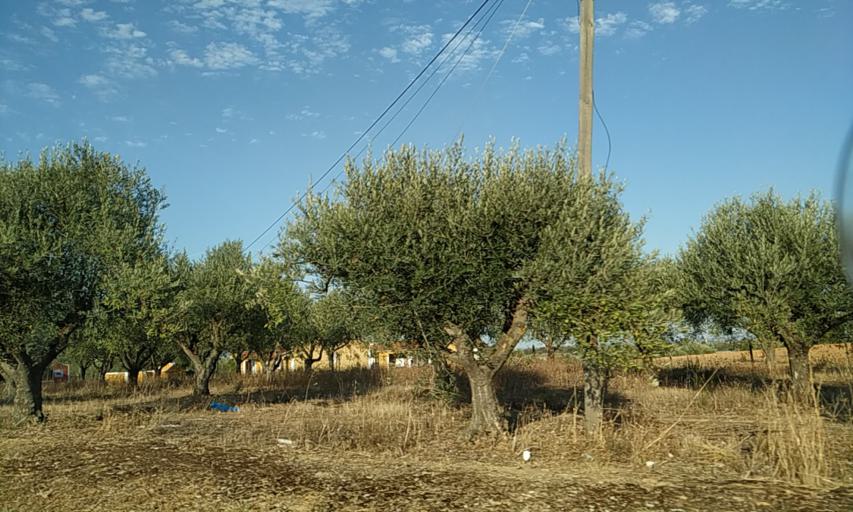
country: PT
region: Santarem
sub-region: Alcanena
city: Alcanena
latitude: 39.4182
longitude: -8.6363
